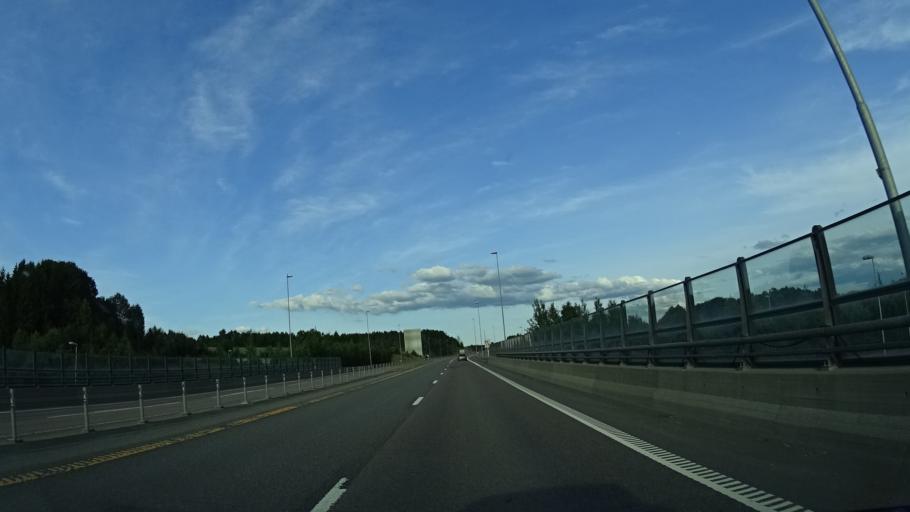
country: NO
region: Ostfold
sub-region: Askim
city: Askim
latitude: 59.5704
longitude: 11.1662
